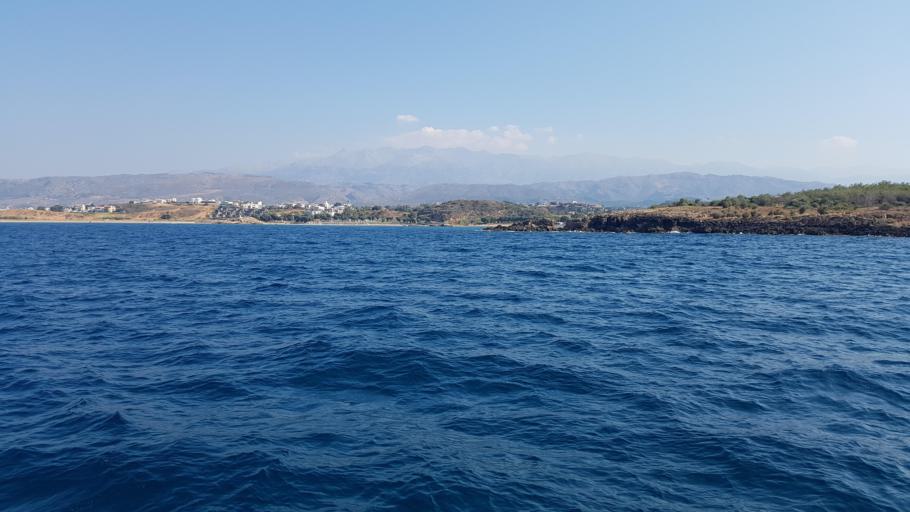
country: GR
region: Crete
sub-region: Nomos Chanias
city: Daratsos
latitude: 35.5195
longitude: 23.9906
